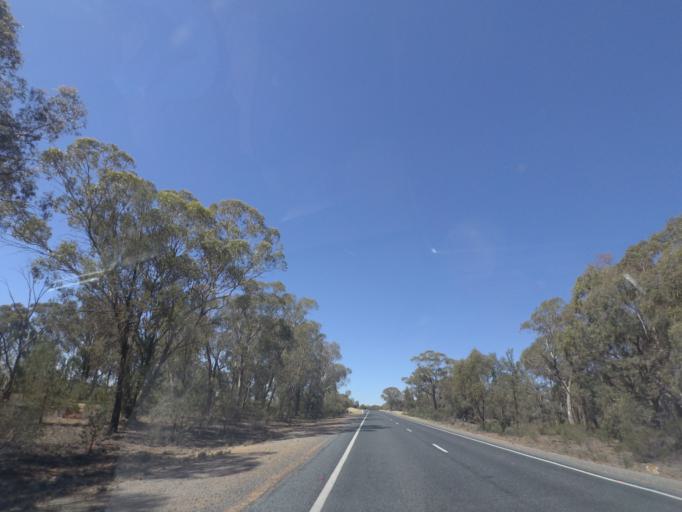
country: AU
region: New South Wales
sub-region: Narrandera
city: Narrandera
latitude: -34.4440
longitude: 146.8404
